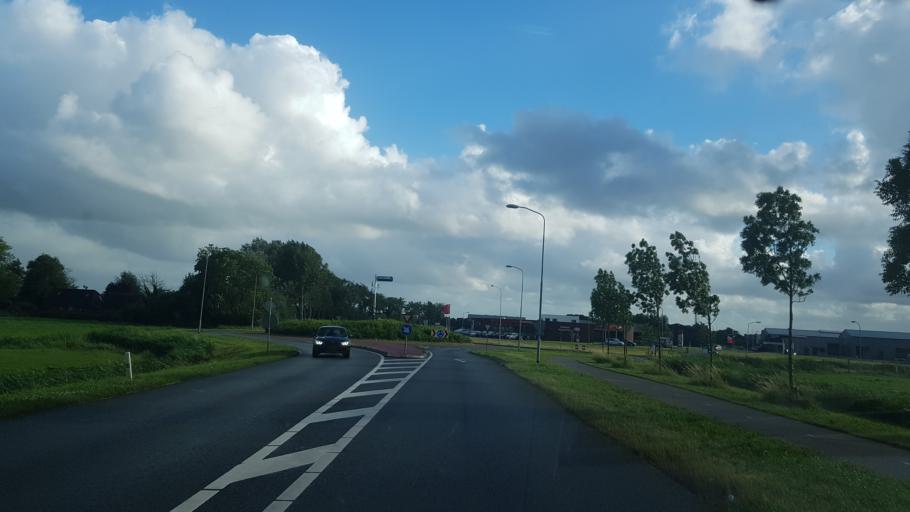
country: NL
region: Groningen
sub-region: Gemeente Bedum
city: Bedum
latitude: 53.2828
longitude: 6.7100
